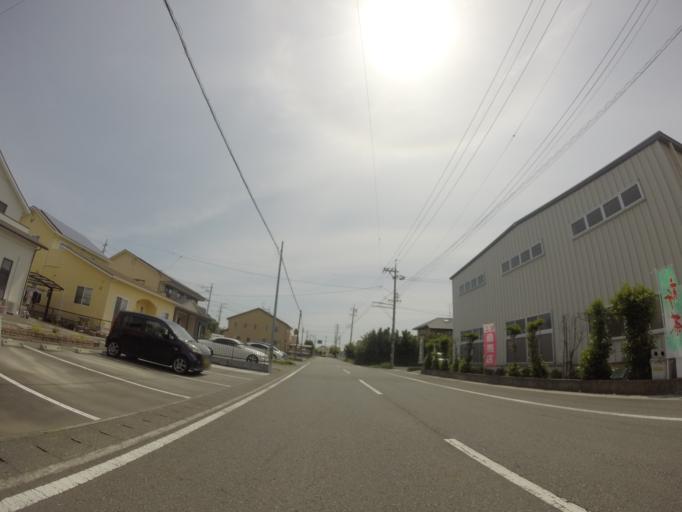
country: JP
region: Shizuoka
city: Fujieda
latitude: 34.8192
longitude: 138.2732
